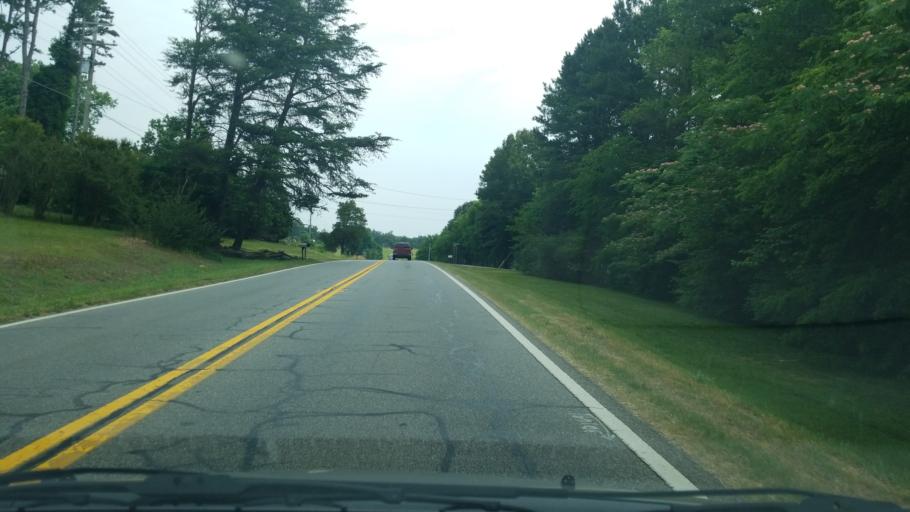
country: US
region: Georgia
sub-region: Catoosa County
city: Ringgold
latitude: 34.8788
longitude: -85.1392
